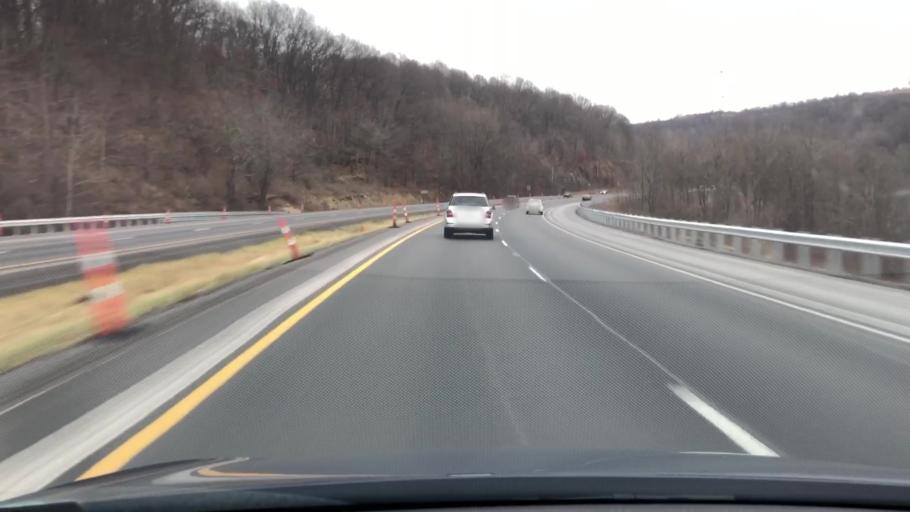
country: US
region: West Virginia
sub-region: Monongalia County
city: Star City
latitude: 39.6737
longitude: -80.0316
